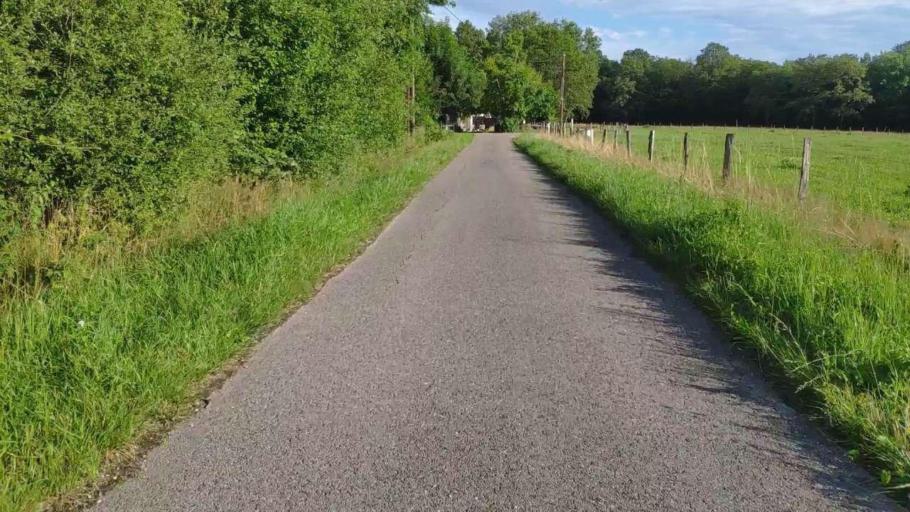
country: FR
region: Franche-Comte
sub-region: Departement du Jura
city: Bletterans
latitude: 46.7803
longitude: 5.4812
